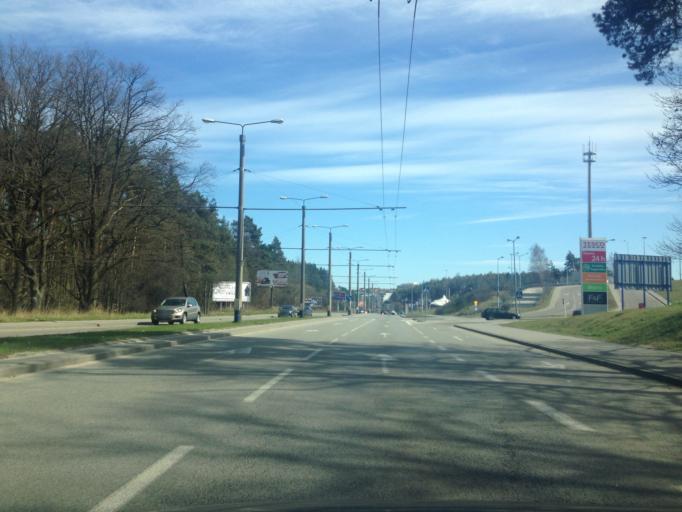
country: PL
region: Pomeranian Voivodeship
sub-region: Gdynia
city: Wielki Kack
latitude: 54.4753
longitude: 18.4742
